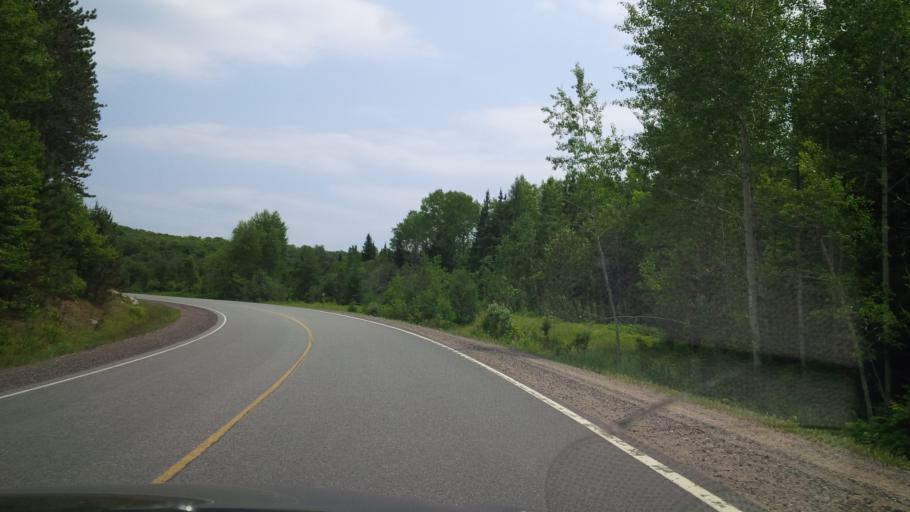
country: CA
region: Ontario
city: Huntsville
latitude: 45.5312
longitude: -79.2979
